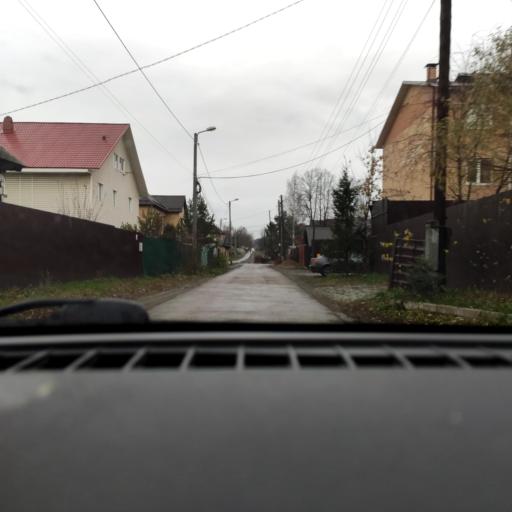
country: RU
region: Perm
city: Kondratovo
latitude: 58.0381
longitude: 56.1172
